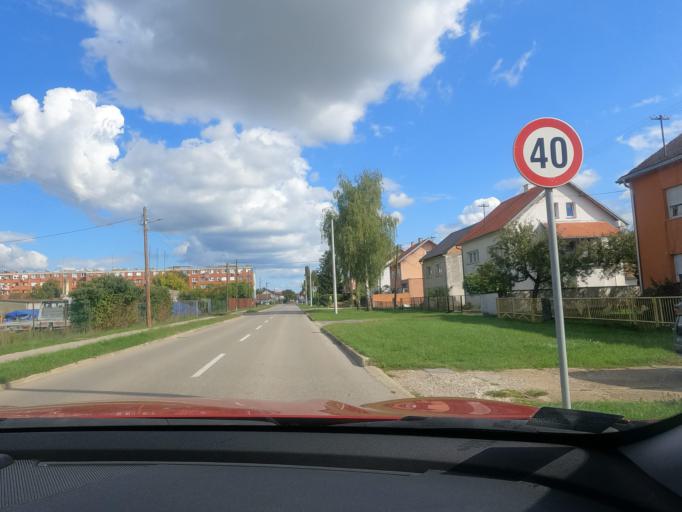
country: HR
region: Sisacko-Moslavacka
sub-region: Grad Sisak
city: Sisak
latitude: 45.4992
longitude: 16.3673
